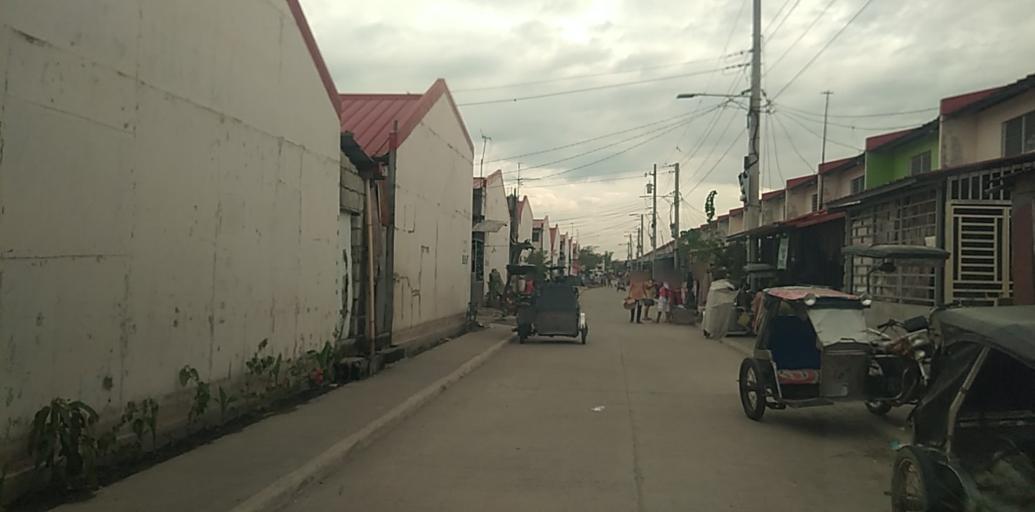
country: PH
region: Central Luzon
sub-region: Province of Pampanga
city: San Fernando
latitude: 15.0088
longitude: 120.7011
